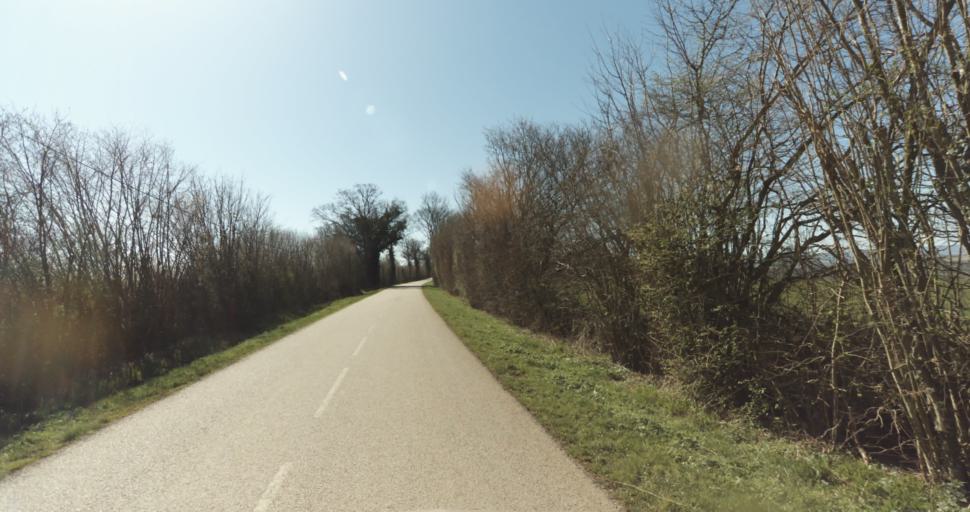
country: FR
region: Lower Normandy
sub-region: Departement de l'Orne
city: Trun
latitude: 48.9193
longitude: 0.0643
